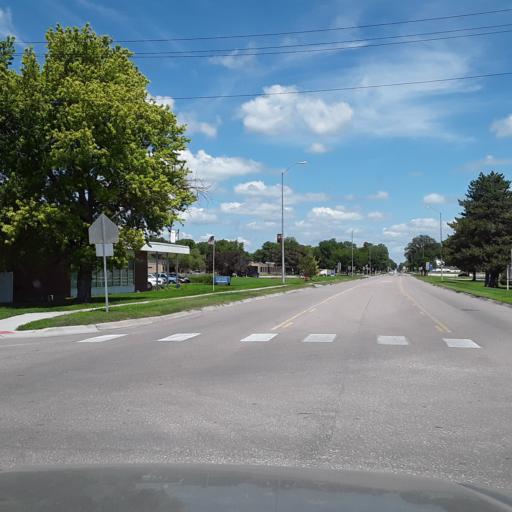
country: US
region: Nebraska
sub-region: Merrick County
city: Central City
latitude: 41.1047
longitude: -98.0018
